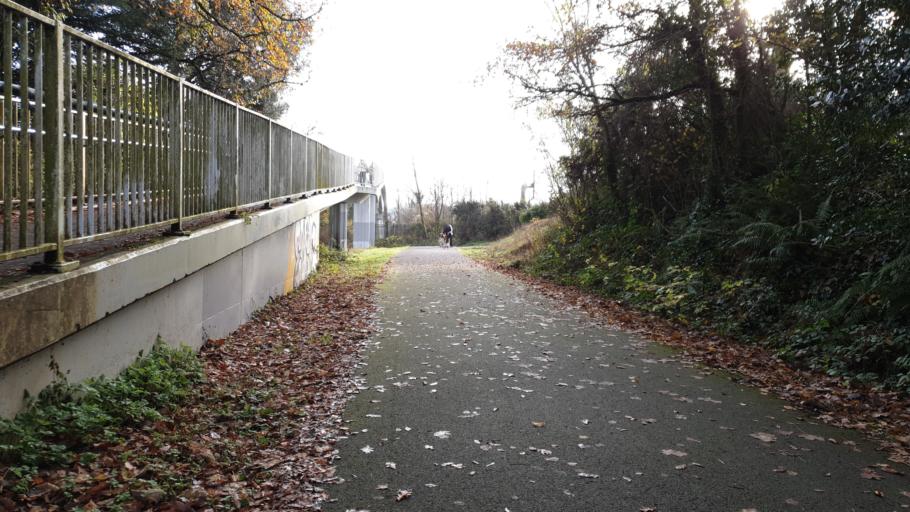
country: IE
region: Munster
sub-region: County Cork
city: Passage West
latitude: 51.8837
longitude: -8.4045
